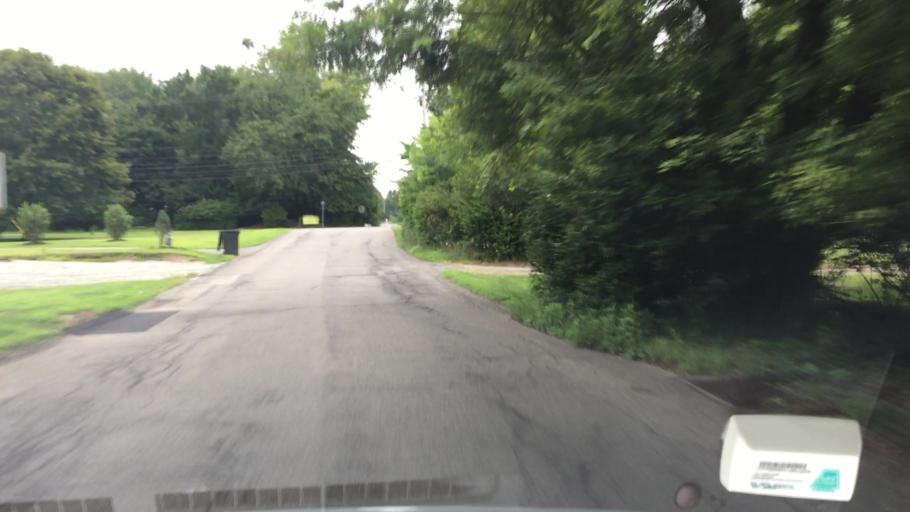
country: US
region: Pennsylvania
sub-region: Allegheny County
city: Allison Park
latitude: 40.5745
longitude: -79.9249
